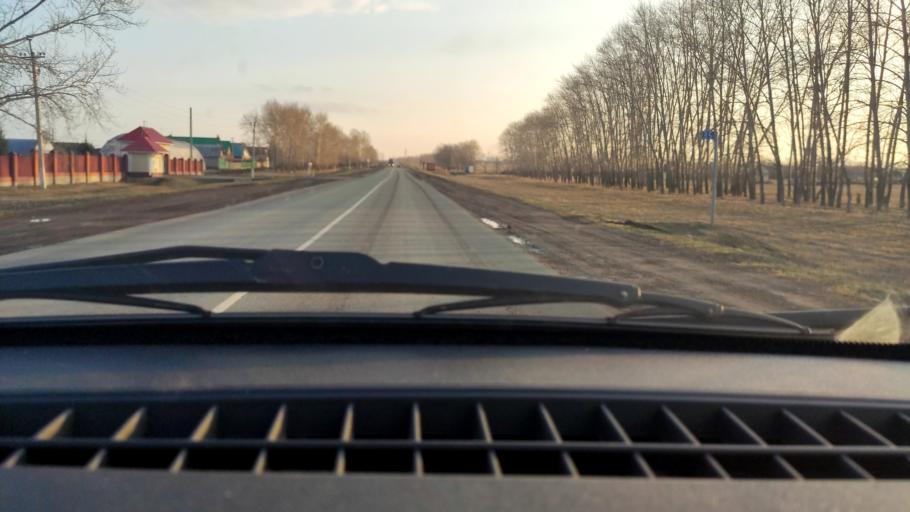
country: RU
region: Bashkortostan
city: Davlekanovo
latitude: 54.3926
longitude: 55.2048
